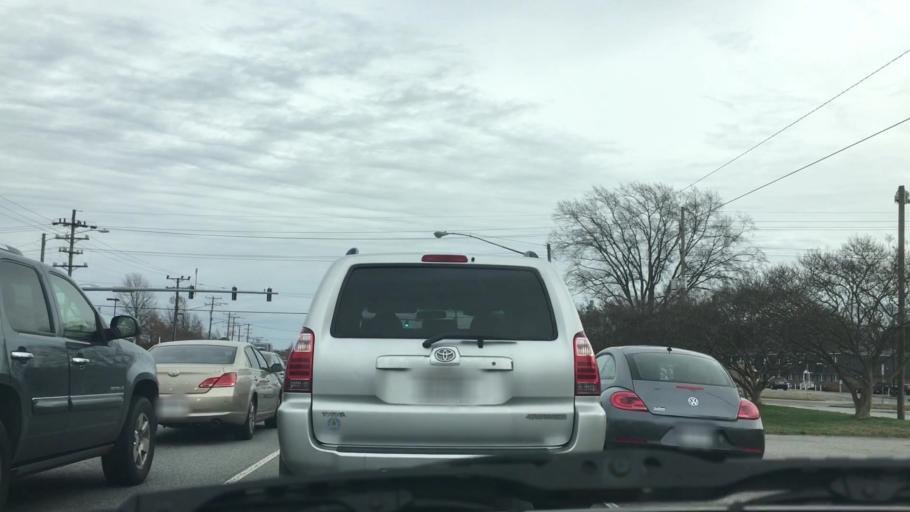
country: US
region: Virginia
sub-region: City of Norfolk
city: Norfolk
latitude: 36.9151
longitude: -76.2215
